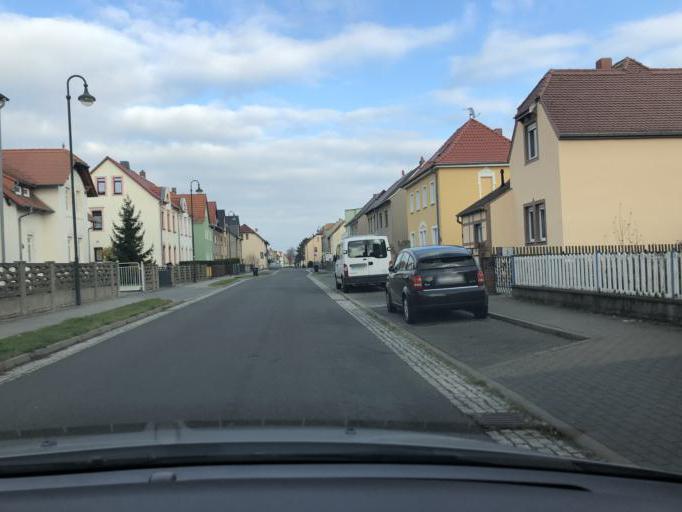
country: DE
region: Saxony
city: Nerchau
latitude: 51.2738
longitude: 12.7916
